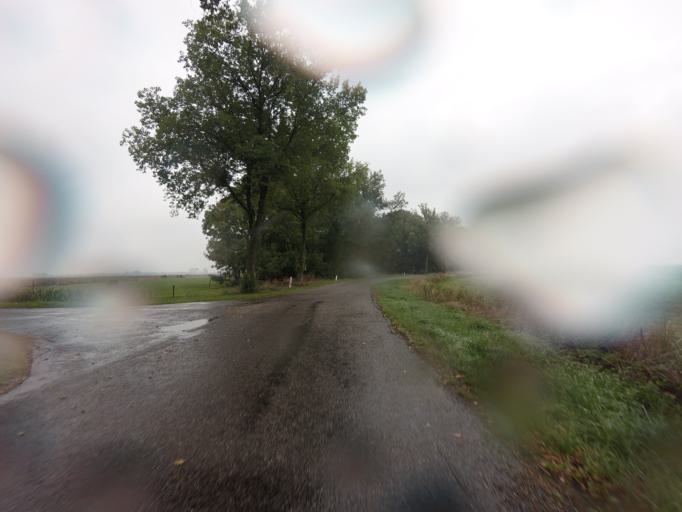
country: NL
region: Friesland
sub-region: Gemeente Boarnsterhim
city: Aldeboarn
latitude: 53.0742
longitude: 5.9284
